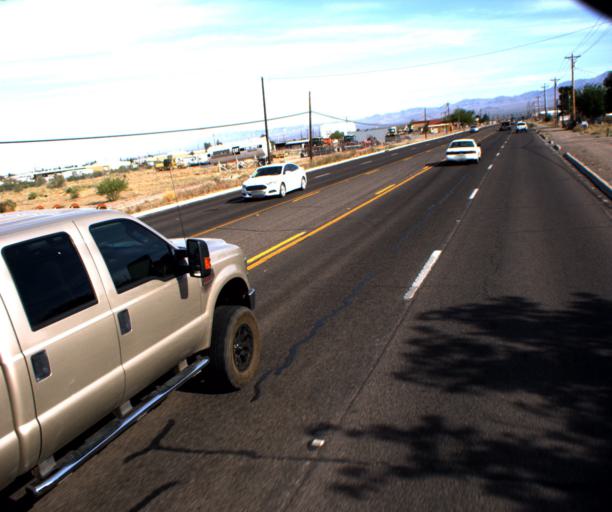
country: US
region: Arizona
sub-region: Graham County
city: Safford
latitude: 32.7968
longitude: -109.7077
